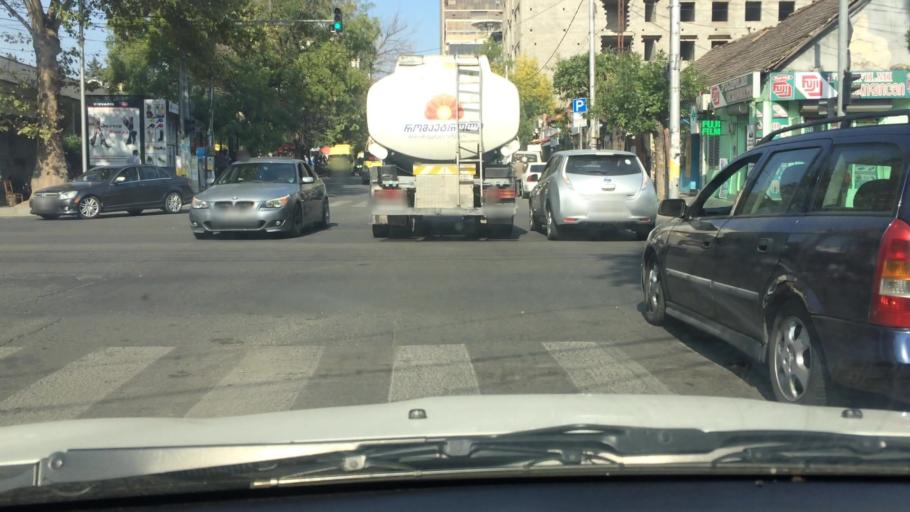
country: GE
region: T'bilisi
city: Tbilisi
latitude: 41.6873
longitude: 44.8276
